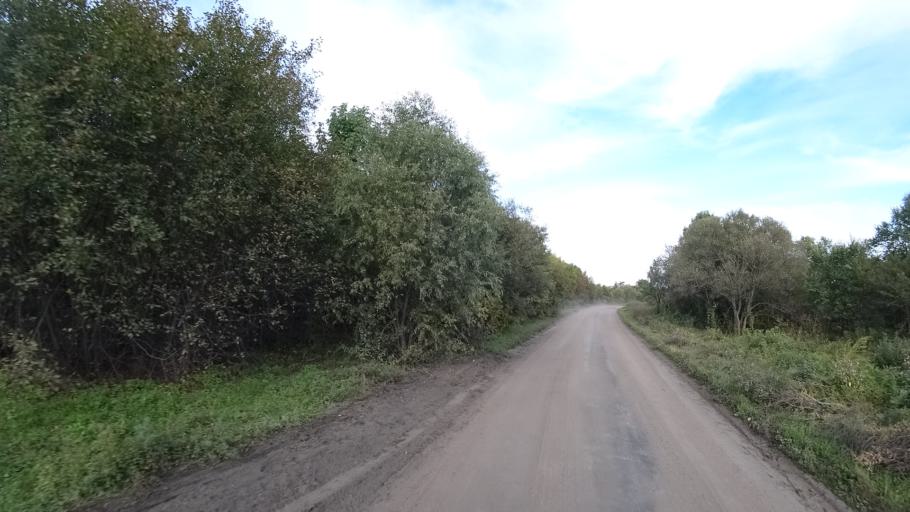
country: RU
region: Amur
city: Arkhara
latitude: 49.3560
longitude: 130.1107
